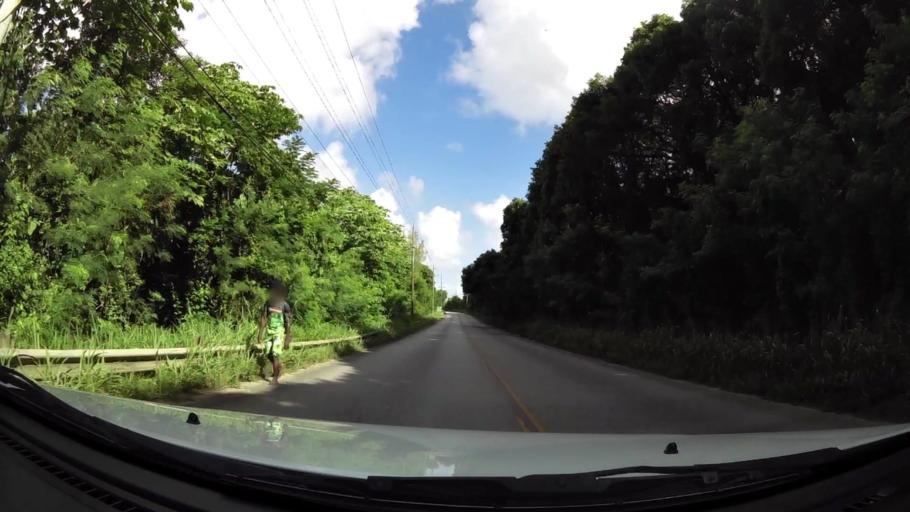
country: BB
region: Saint Peter
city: Speightstown
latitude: 13.2341
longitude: -59.6232
